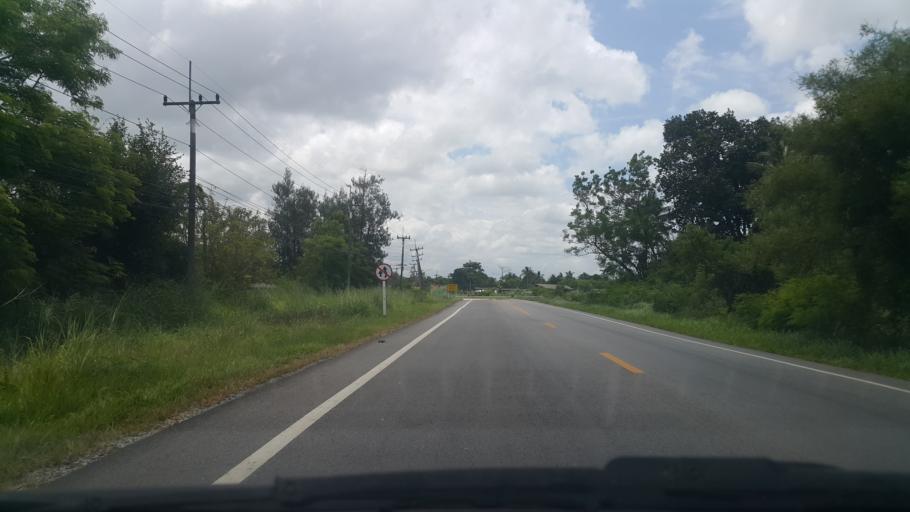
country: TH
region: Rayong
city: Ban Chang
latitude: 12.7863
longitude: 101.0275
